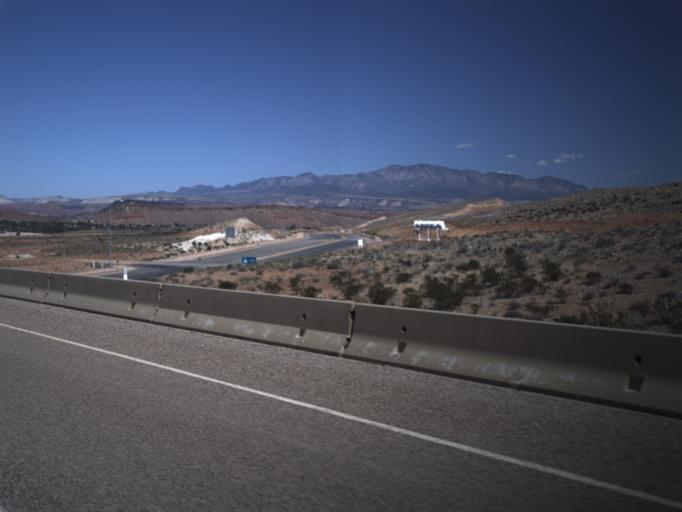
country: US
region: Utah
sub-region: Washington County
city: Saint George
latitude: 37.0247
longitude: -113.6013
